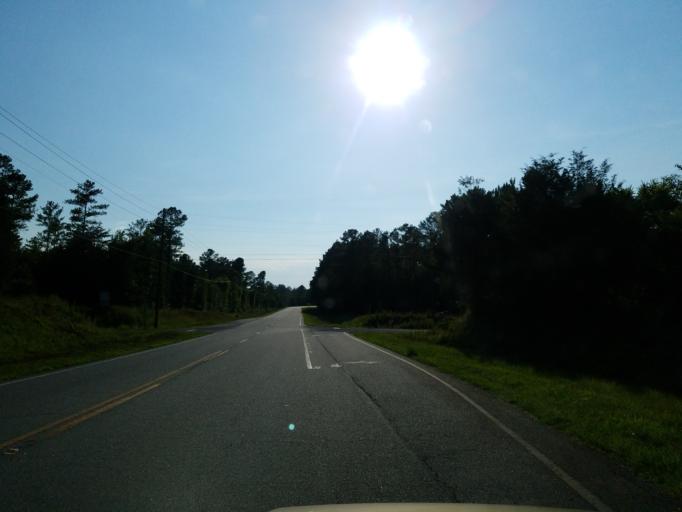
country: US
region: Georgia
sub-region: Bartow County
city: Rydal
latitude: 34.3381
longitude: -84.7342
